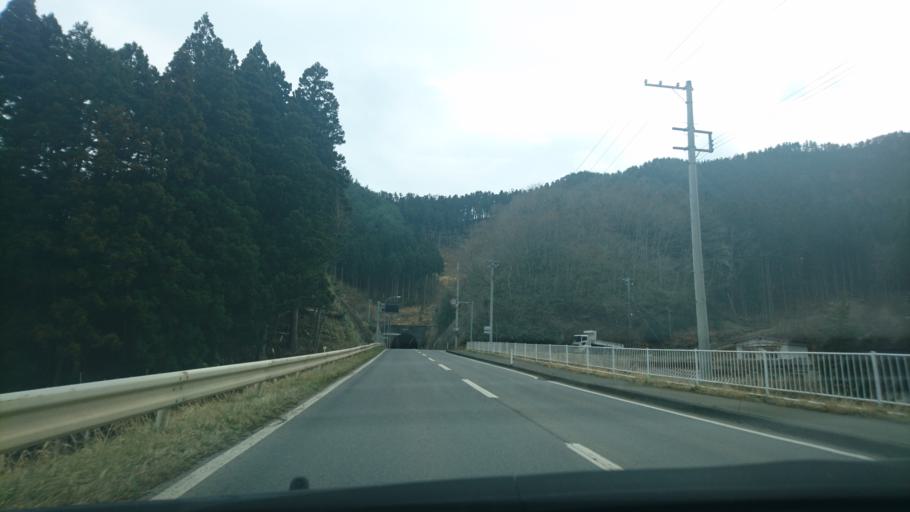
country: JP
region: Iwate
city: Kamaishi
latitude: 39.2004
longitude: 141.8612
